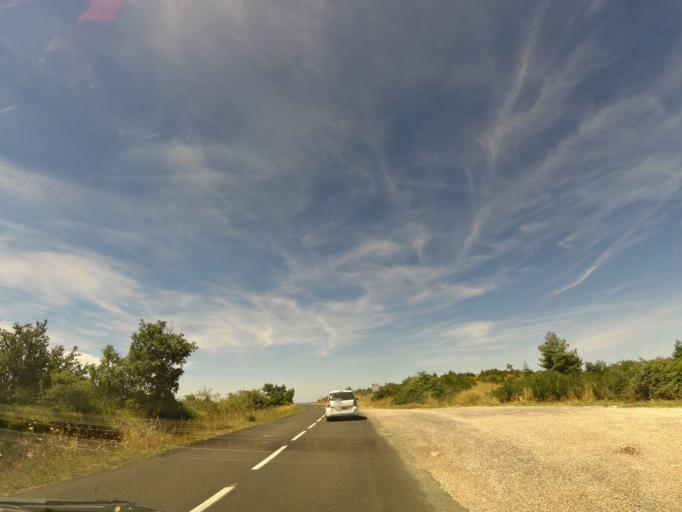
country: FR
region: Midi-Pyrenees
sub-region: Departement de l'Aveyron
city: La Cavalerie
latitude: 43.9664
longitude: 3.3337
